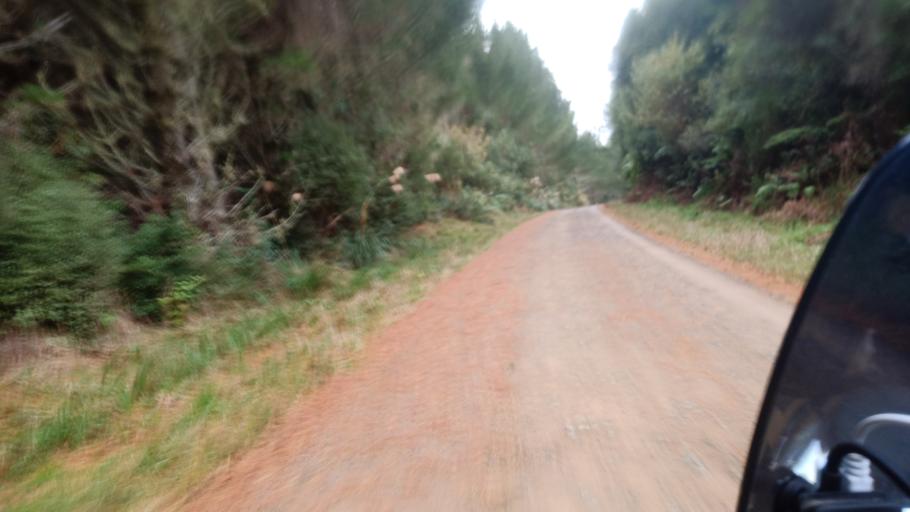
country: NZ
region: Bay of Plenty
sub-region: Whakatane District
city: Murupara
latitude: -38.6659
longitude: 176.6284
